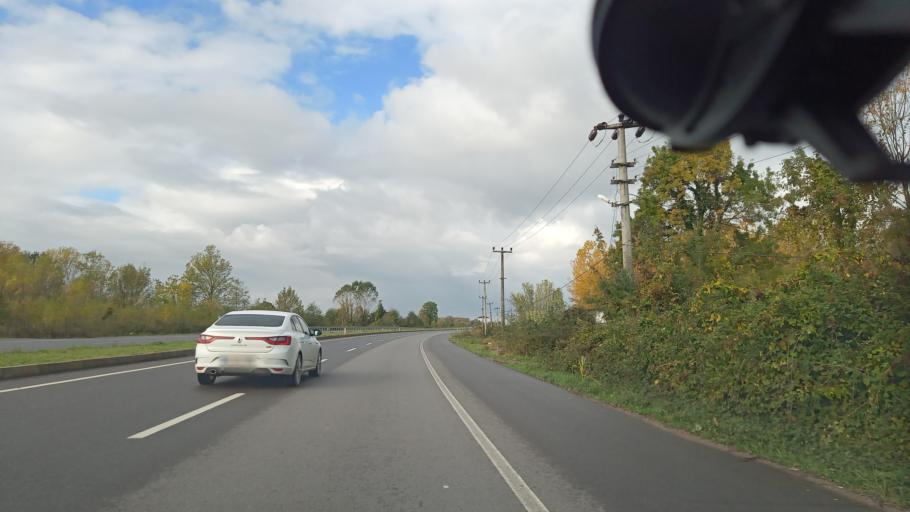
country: TR
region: Sakarya
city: Karasu
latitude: 41.0700
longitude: 30.7975
